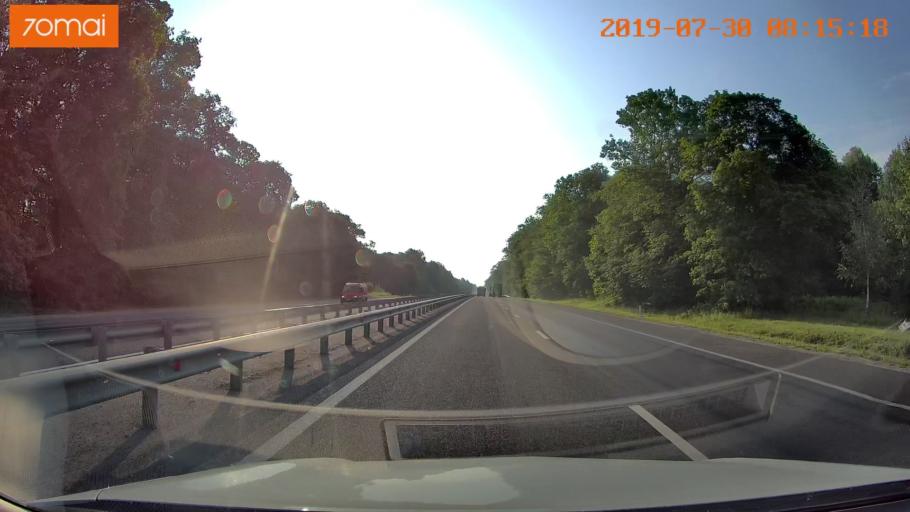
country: RU
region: Kaliningrad
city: Zheleznodorozhnyy
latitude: 54.6451
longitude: 21.3816
